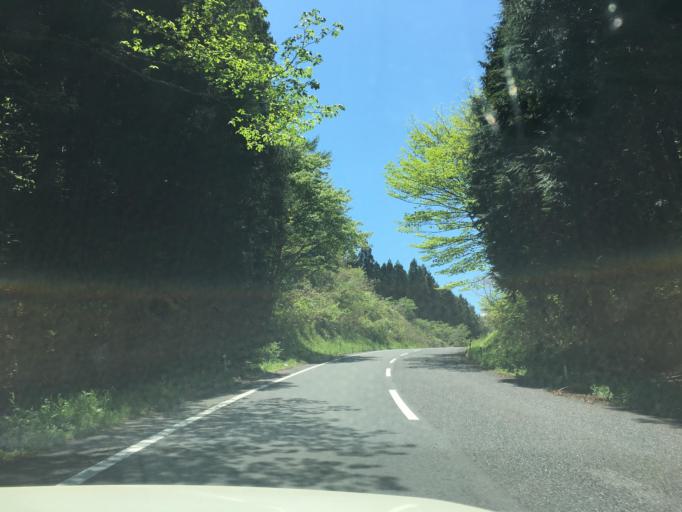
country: JP
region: Fukushima
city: Funehikimachi-funehiki
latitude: 37.3874
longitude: 140.6102
